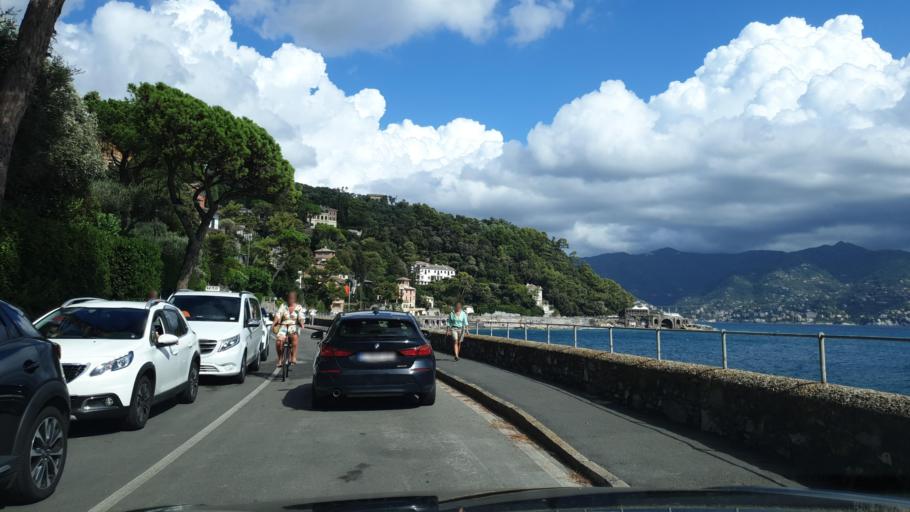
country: IT
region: Liguria
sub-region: Provincia di Genova
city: Portofino
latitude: 44.3170
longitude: 9.2117
